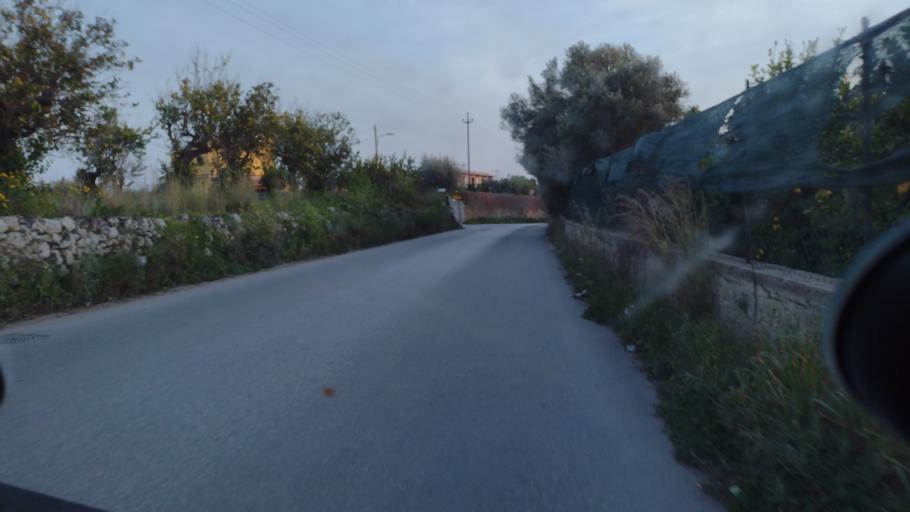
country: IT
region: Sicily
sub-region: Provincia di Siracusa
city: Avola
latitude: 36.8812
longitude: 15.1307
